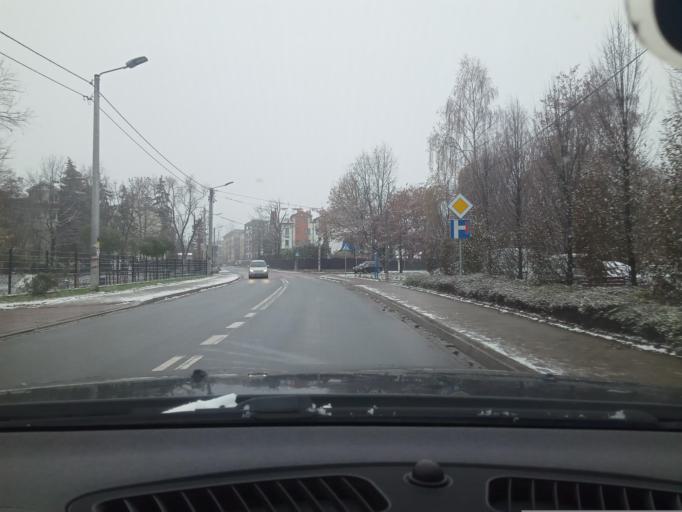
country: PL
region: Lesser Poland Voivodeship
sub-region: Krakow
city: Sidzina
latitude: 50.0152
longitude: 19.8961
